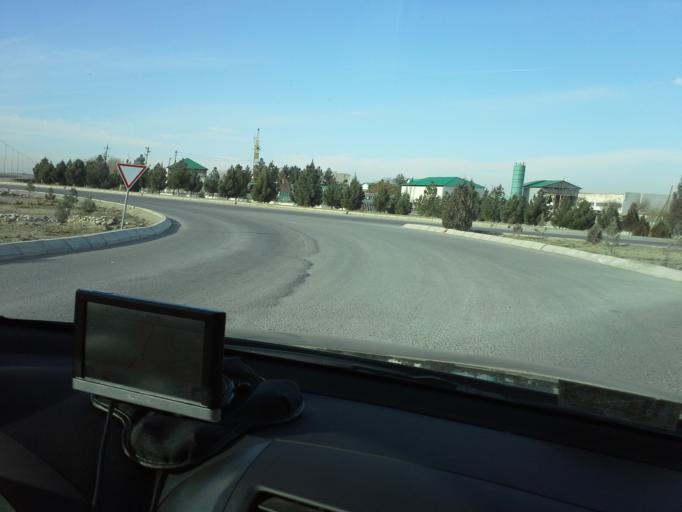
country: TM
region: Ahal
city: Abadan
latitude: 38.0215
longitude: 58.1799
